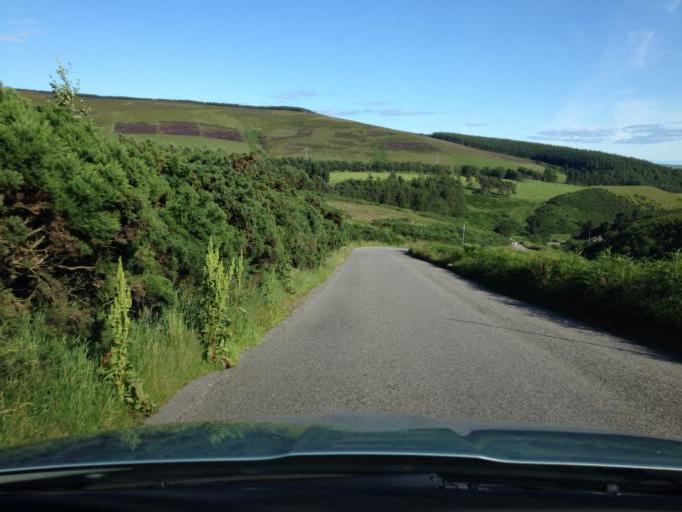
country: GB
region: Scotland
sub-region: Aberdeenshire
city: Laurencekirk
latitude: 56.8974
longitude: -2.5568
